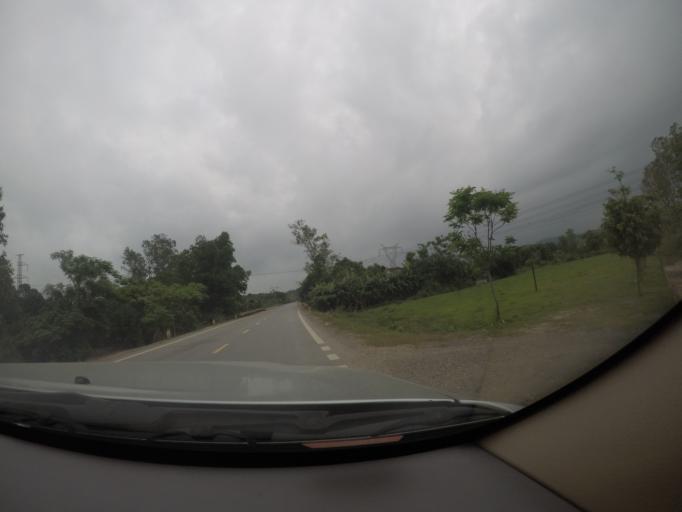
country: VN
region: Quang Binh
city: Kien Giang
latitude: 17.1785
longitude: 106.7371
